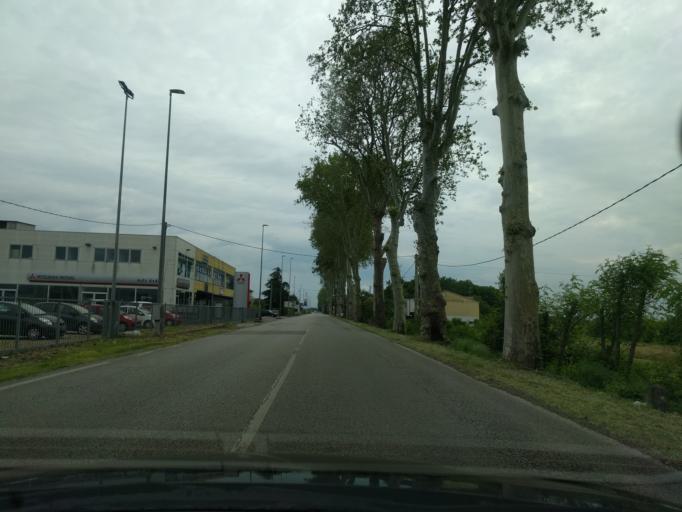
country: IT
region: Veneto
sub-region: Provincia di Rovigo
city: Rovigo
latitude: 45.0435
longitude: 11.7836
